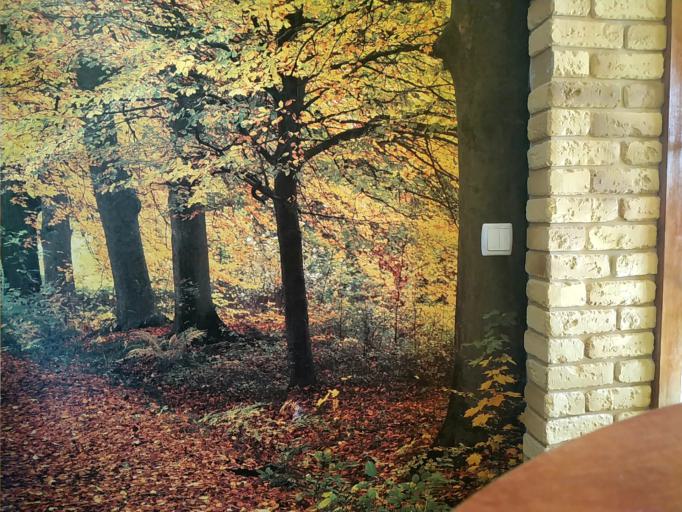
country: RU
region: Jaroslavl
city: Kukoboy
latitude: 58.8562
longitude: 39.7328
